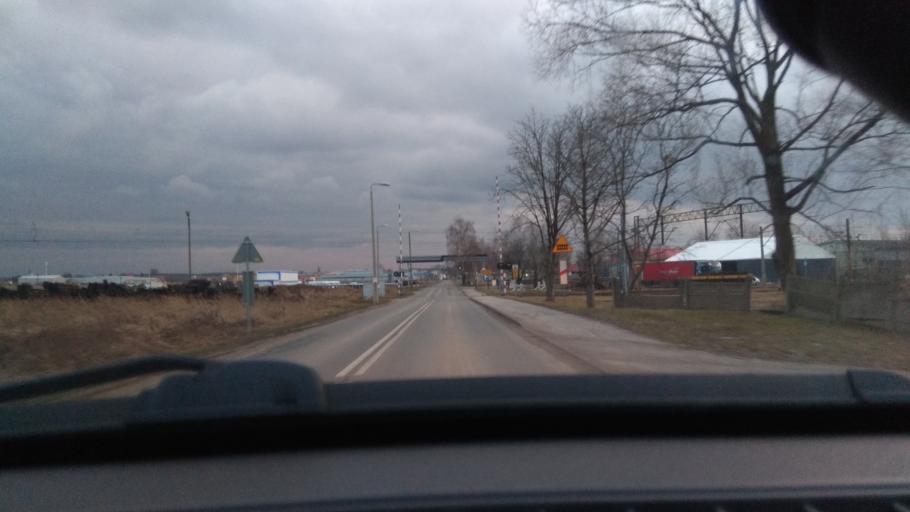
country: PL
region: Greater Poland Voivodeship
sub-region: Powiat kepinski
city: Kepno
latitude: 51.2938
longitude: 18.0061
